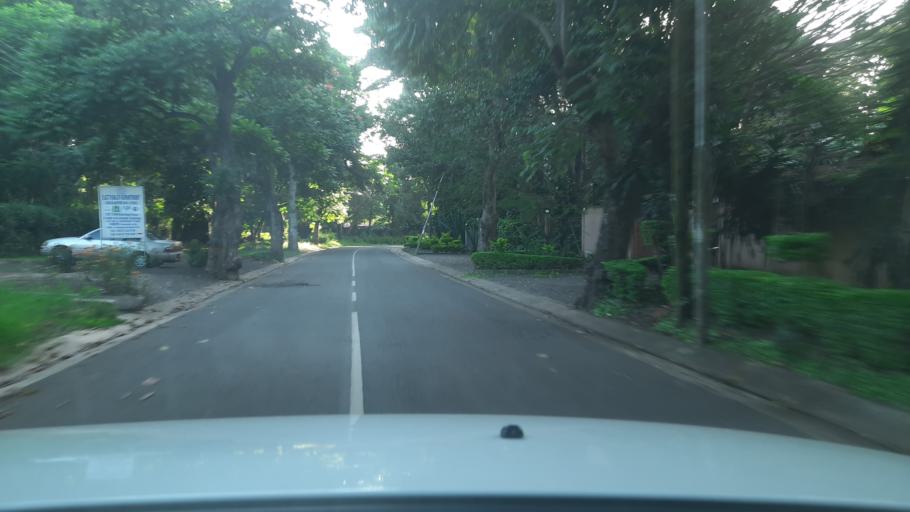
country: TZ
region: Arusha
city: Arusha
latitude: -3.3801
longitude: 36.6984
